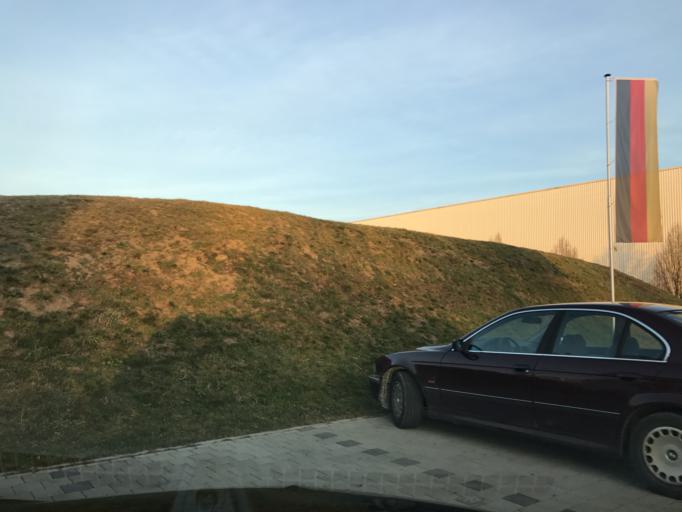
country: DE
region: Baden-Wuerttemberg
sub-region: Tuebingen Region
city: Friedrichshafen
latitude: 47.6704
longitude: 9.4983
